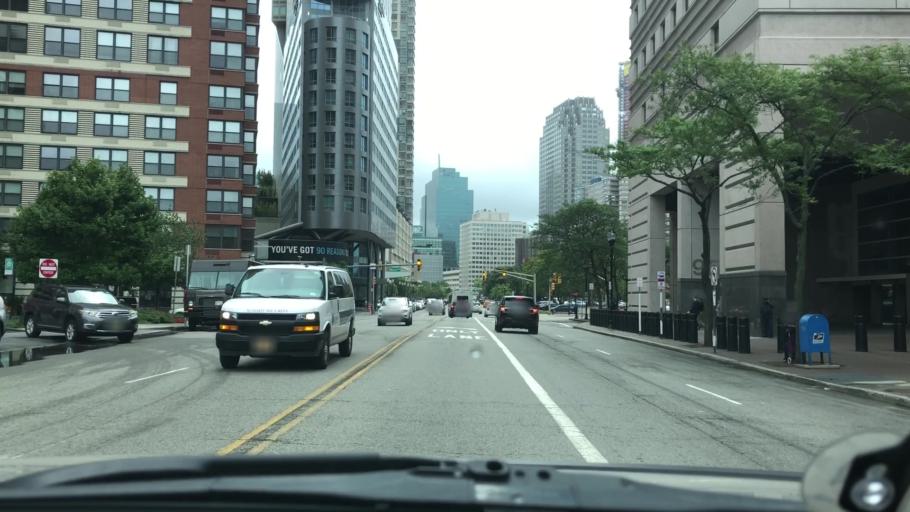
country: US
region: New Jersey
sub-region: Hudson County
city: Hoboken
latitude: 40.7194
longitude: -74.0425
